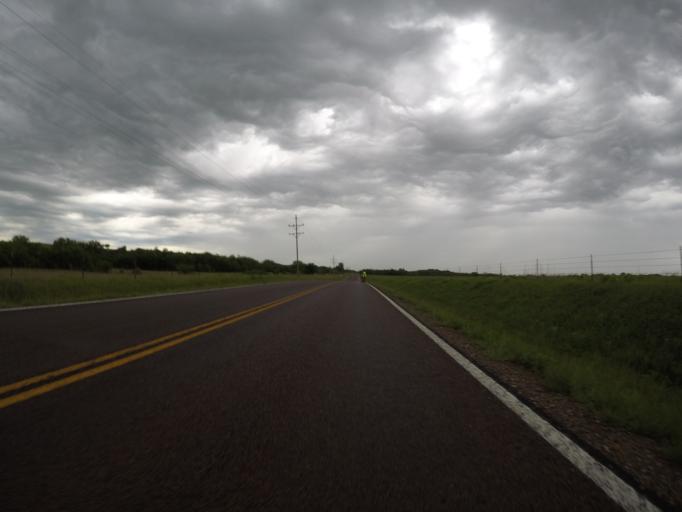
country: US
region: Kansas
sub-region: Shawnee County
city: Rossville
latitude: 38.9573
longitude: -96.0512
